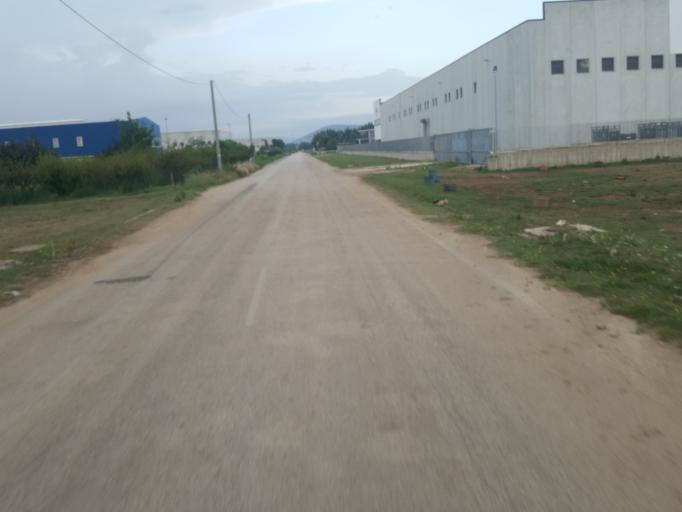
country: IT
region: Campania
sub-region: Provincia di Caserta
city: Pignataro Maggiore
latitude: 41.1749
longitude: 14.1463
